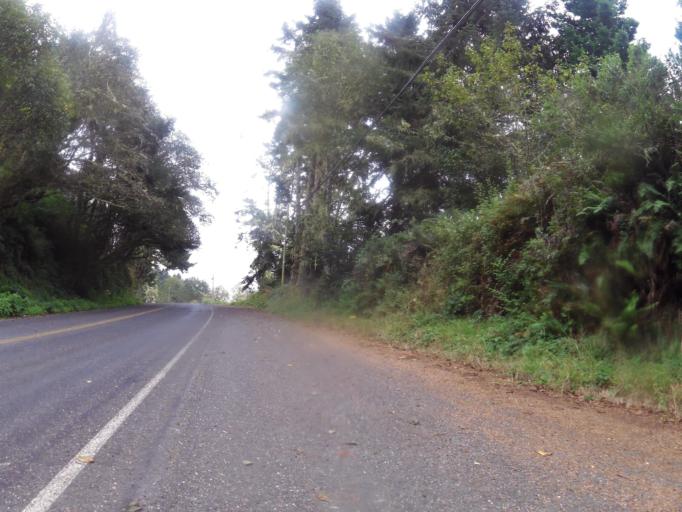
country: US
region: California
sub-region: Humboldt County
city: Westhaven-Moonstone
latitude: 41.1012
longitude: -124.1594
